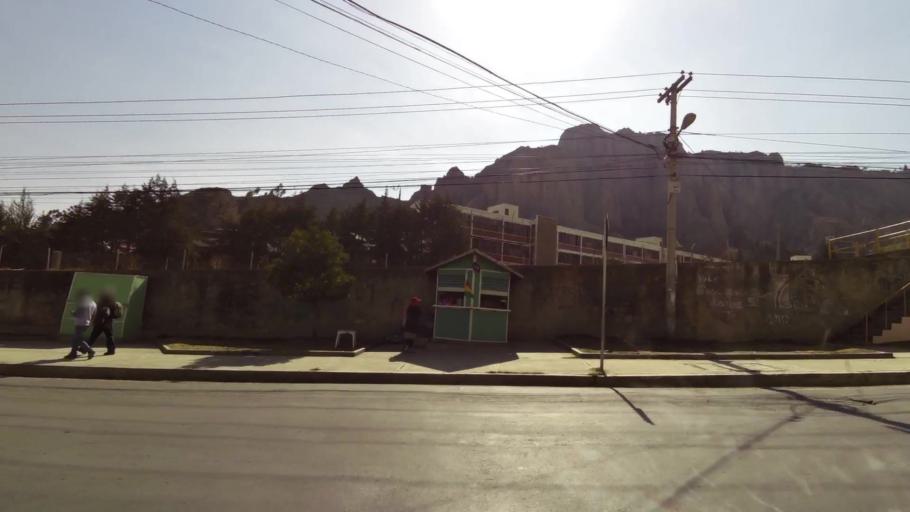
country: BO
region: La Paz
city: La Paz
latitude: -16.5230
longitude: -68.0665
